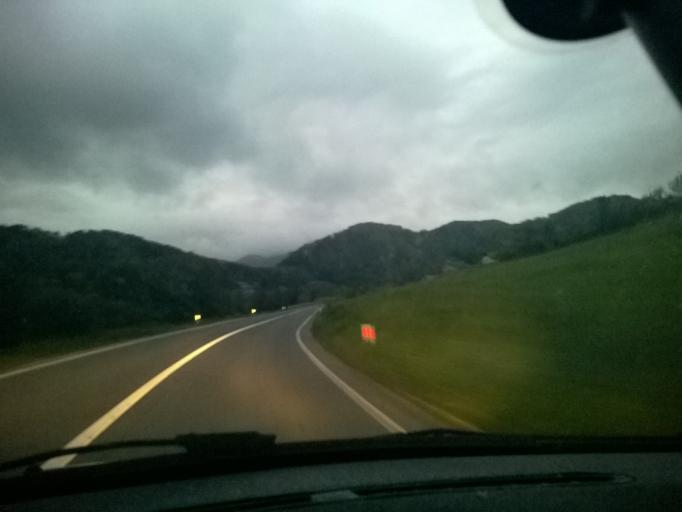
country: HR
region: Krapinsko-Zagorska
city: Pregrada
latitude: 46.2119
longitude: 15.7517
